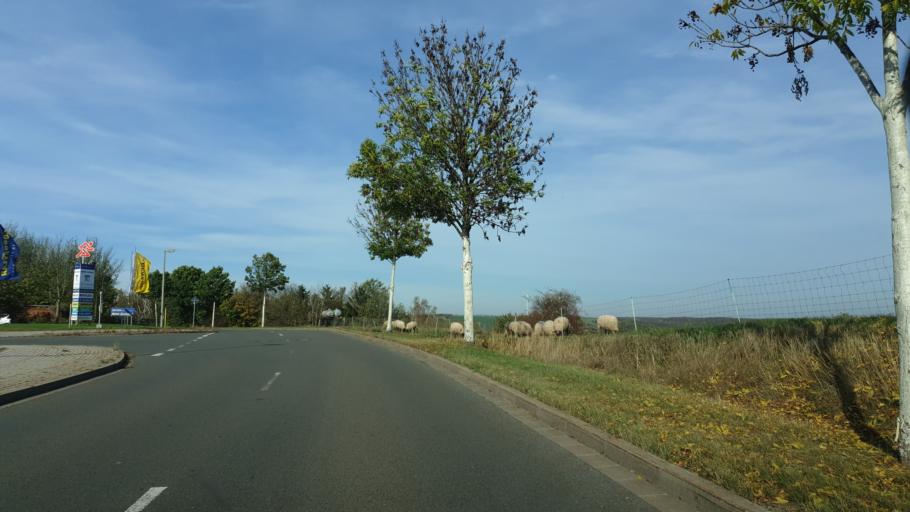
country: DE
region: Thuringia
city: Schwaara
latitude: 50.9039
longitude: 12.1137
